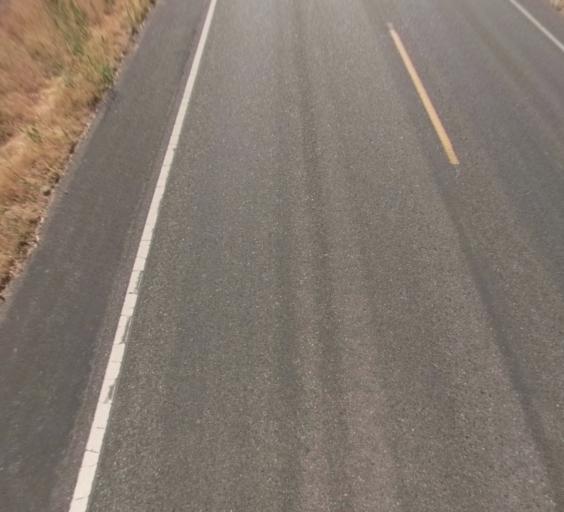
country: US
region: California
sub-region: Madera County
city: Bonadelle Ranchos-Madera Ranchos
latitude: 36.9666
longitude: -119.9443
